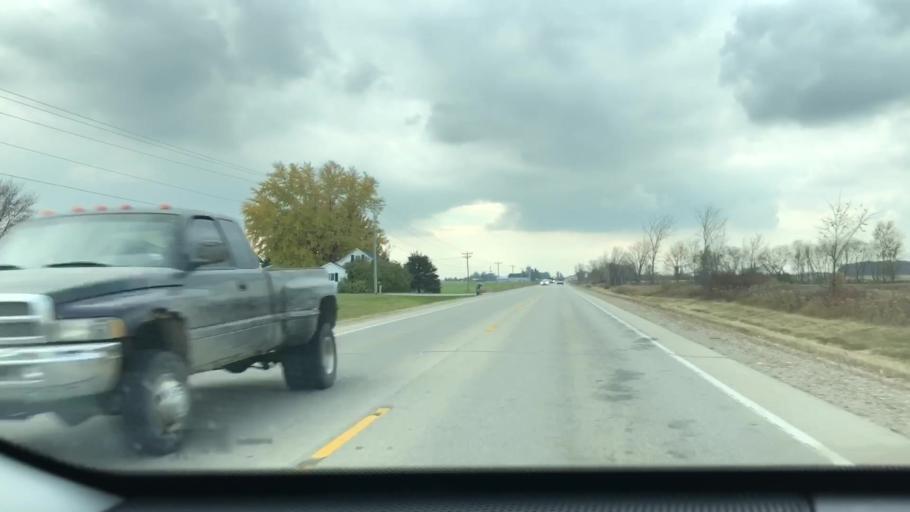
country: US
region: Wisconsin
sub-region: Outagamie County
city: Seymour
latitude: 44.5007
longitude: -88.2830
